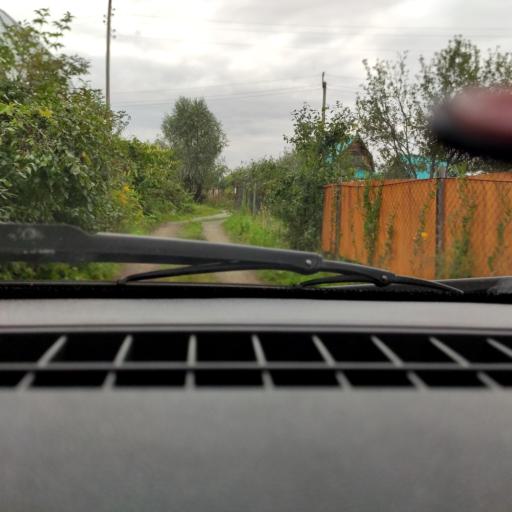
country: RU
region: Bashkortostan
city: Iglino
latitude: 54.7884
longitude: 56.2079
